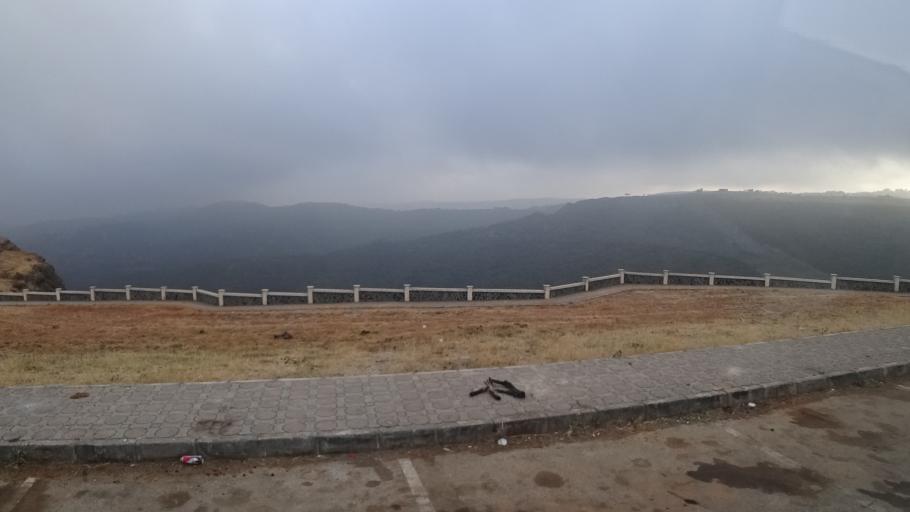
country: OM
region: Zufar
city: Salalah
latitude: 17.1225
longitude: 53.9753
